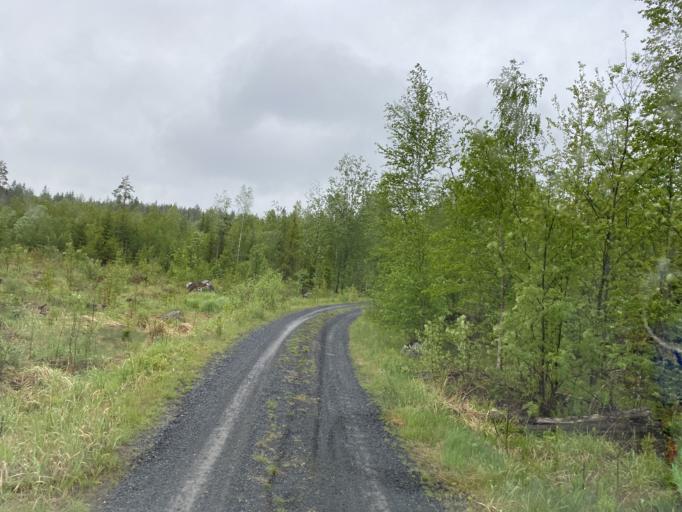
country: FI
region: Pirkanmaa
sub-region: Etelae-Pirkanmaa
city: Urjala
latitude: 60.9540
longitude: 23.5574
